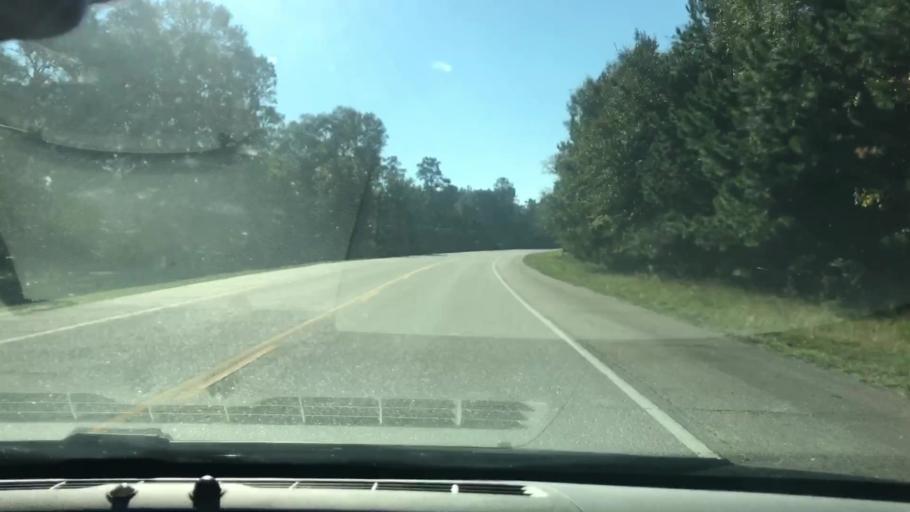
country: US
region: Mississippi
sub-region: Pearl River County
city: Nicholson
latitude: 30.5016
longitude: -89.8152
